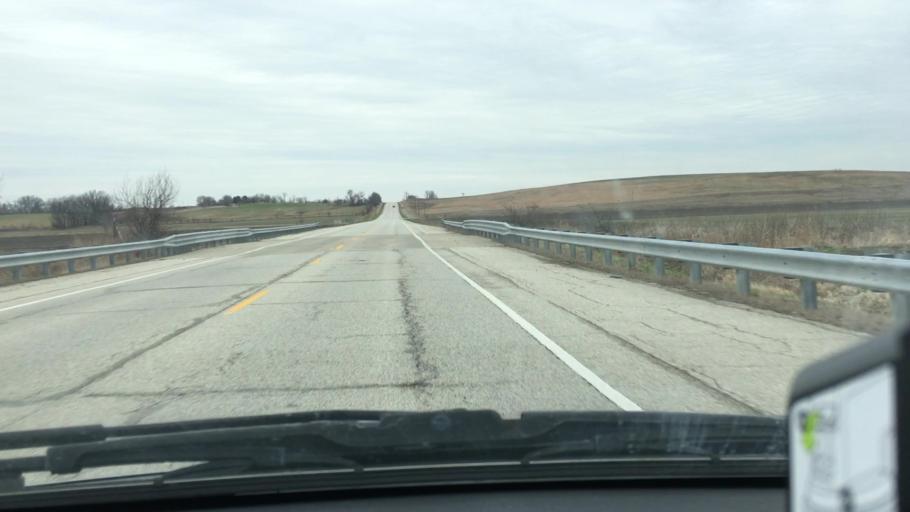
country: US
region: Indiana
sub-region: Greene County
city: Bloomfield
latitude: 39.0060
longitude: -87.0163
